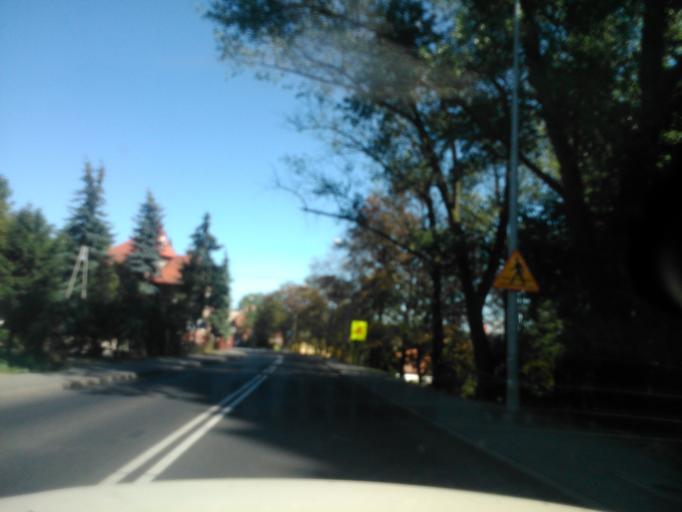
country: PL
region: Kujawsko-Pomorskie
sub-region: Powiat golubsko-dobrzynski
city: Golub-Dobrzyn
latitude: 53.1159
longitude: 19.0500
